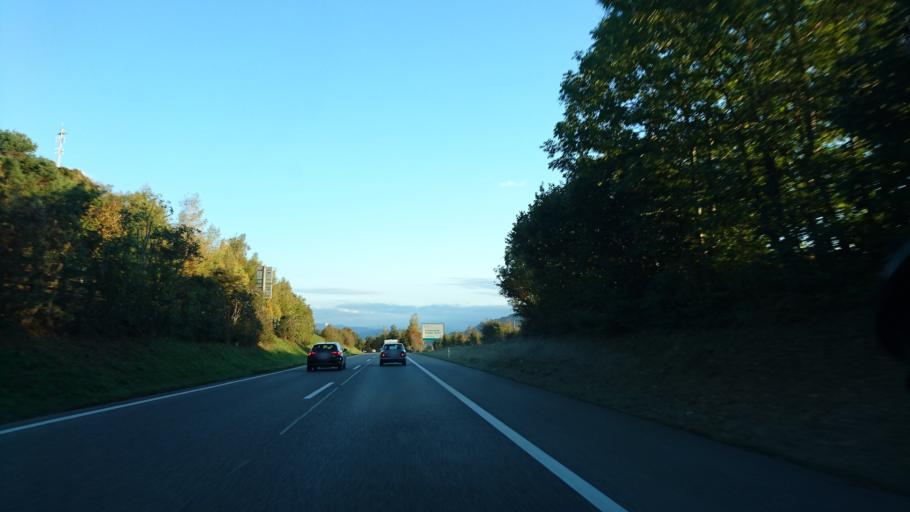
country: CH
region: Bern
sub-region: Bern-Mittelland District
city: Belp
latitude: 46.9149
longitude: 7.5124
